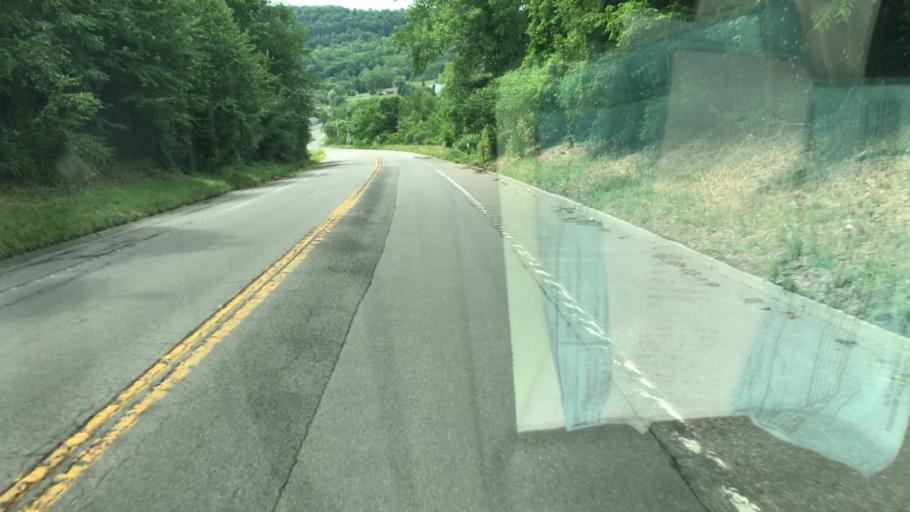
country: US
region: New York
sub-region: Onondaga County
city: Marcellus
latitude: 42.9325
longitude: -76.3232
